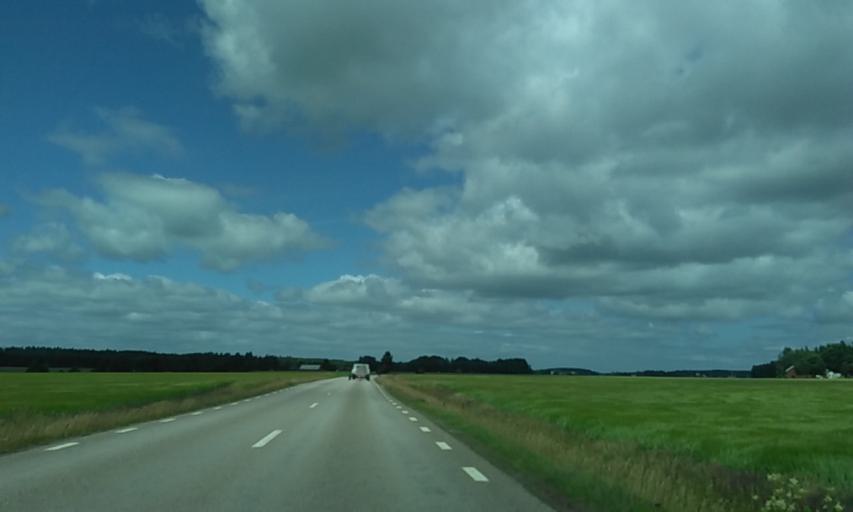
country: SE
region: Vaestra Goetaland
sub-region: Grastorps Kommun
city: Graestorp
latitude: 58.2835
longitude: 12.6732
